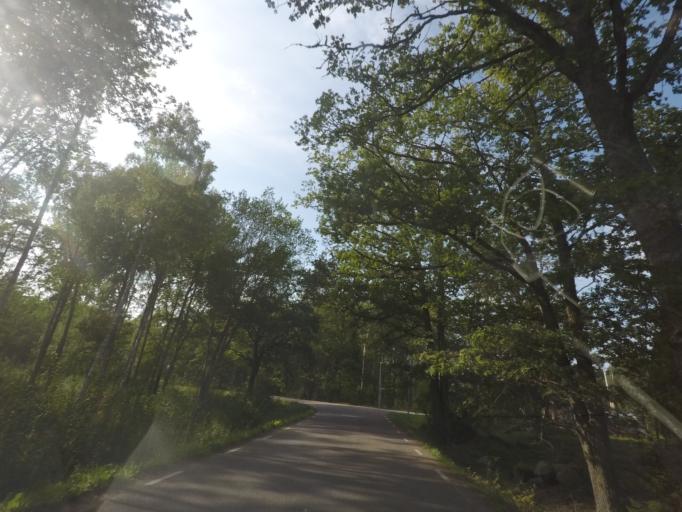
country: SE
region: Vaestmanland
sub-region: Hallstahammars Kommun
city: Kolback
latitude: 59.5284
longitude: 16.2306
